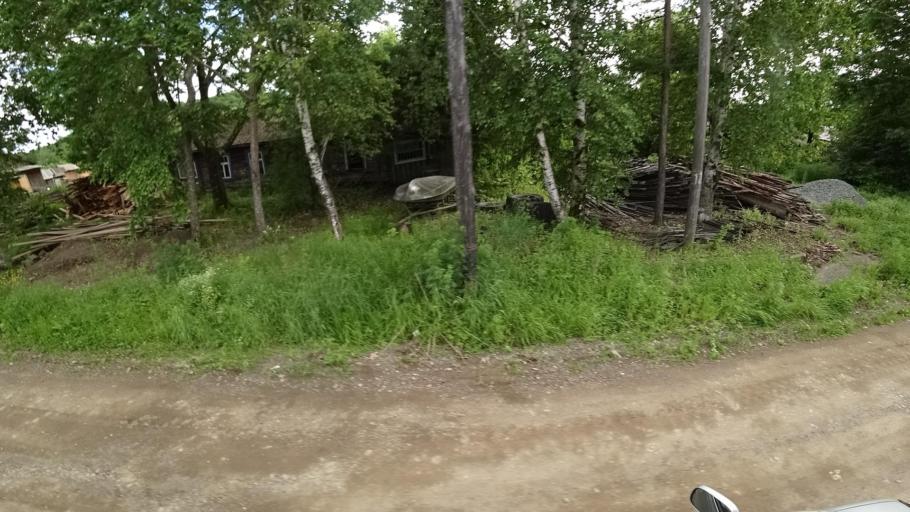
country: RU
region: Khabarovsk Krai
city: Litovko
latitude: 49.3664
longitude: 135.1759
